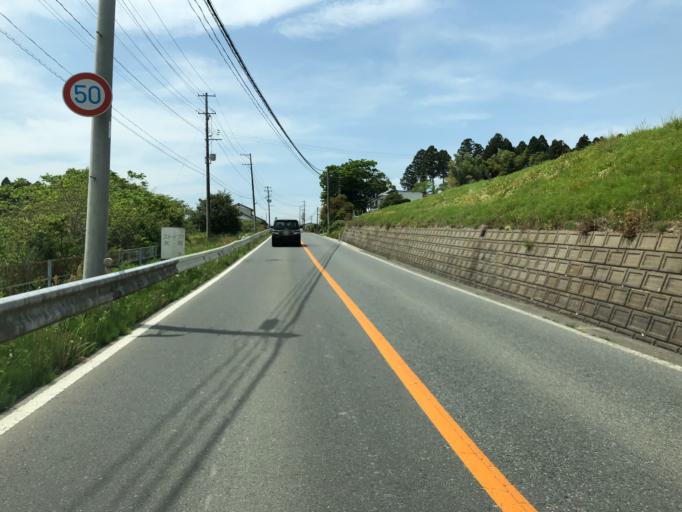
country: JP
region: Fukushima
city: Namie
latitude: 37.6981
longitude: 140.9588
